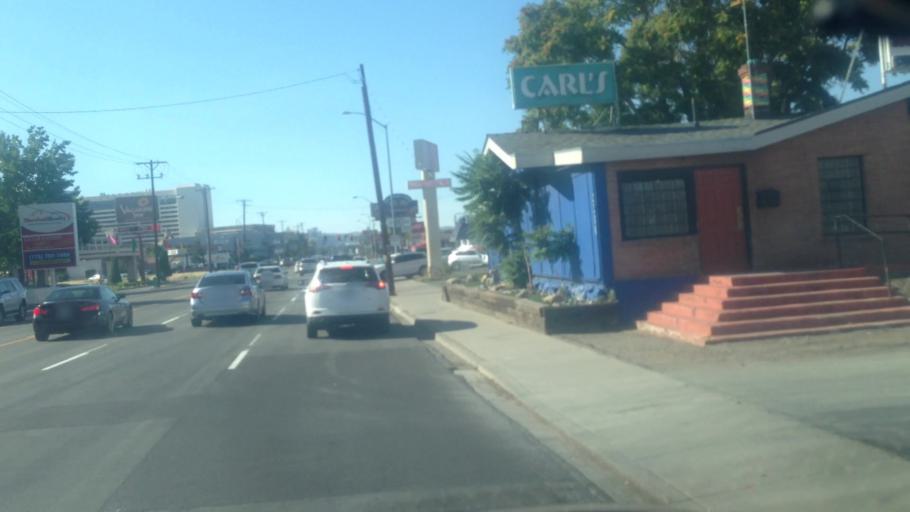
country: US
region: Nevada
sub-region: Washoe County
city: Reno
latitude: 39.4929
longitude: -119.7969
